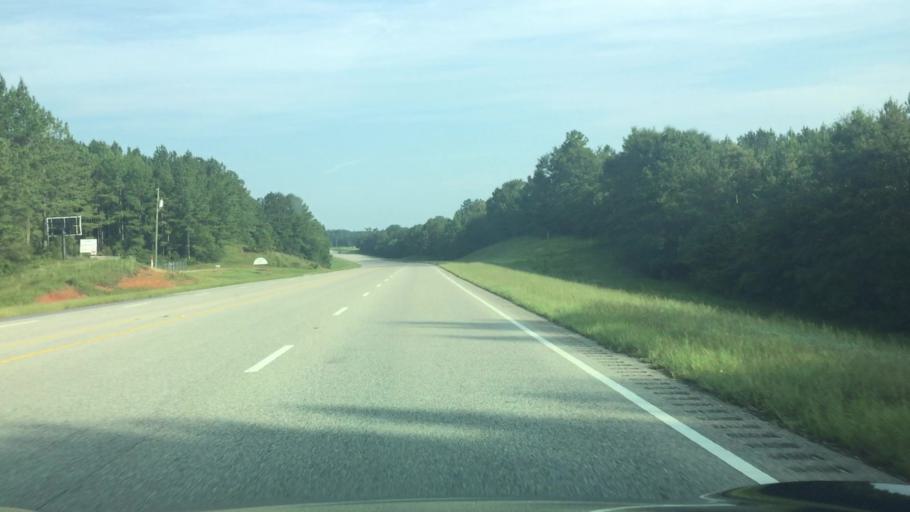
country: US
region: Alabama
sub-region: Butler County
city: Georgiana
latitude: 31.4934
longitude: -86.6876
